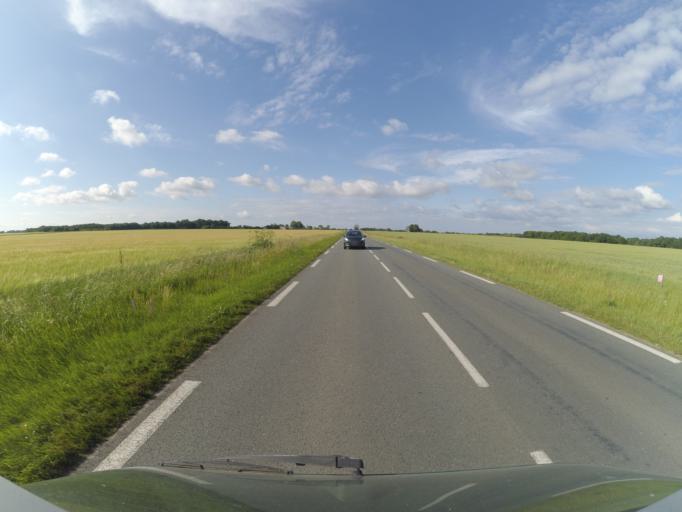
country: FR
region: Poitou-Charentes
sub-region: Departement de la Charente-Maritime
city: Le Gua
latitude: 45.7399
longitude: -0.9502
